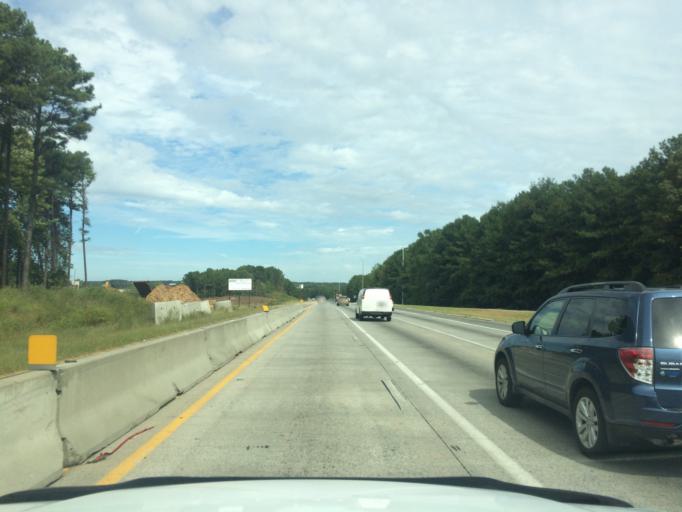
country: US
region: Georgia
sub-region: Cobb County
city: Kennesaw
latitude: 34.0124
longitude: -84.5681
